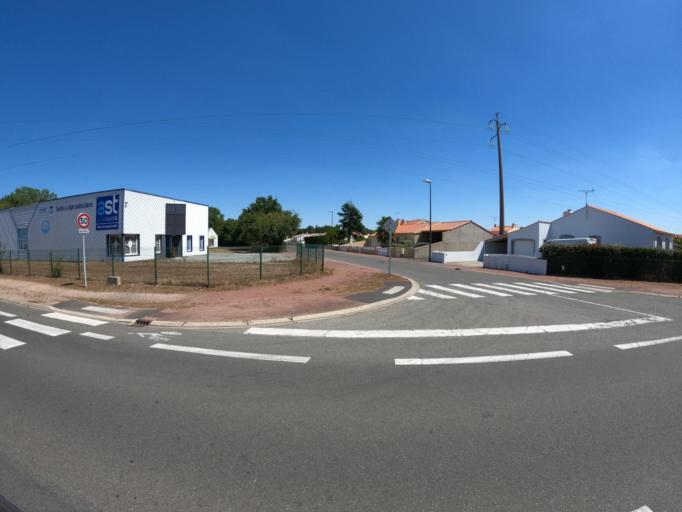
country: FR
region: Pays de la Loire
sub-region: Departement de la Vendee
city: Challans
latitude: 46.8467
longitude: -1.8593
